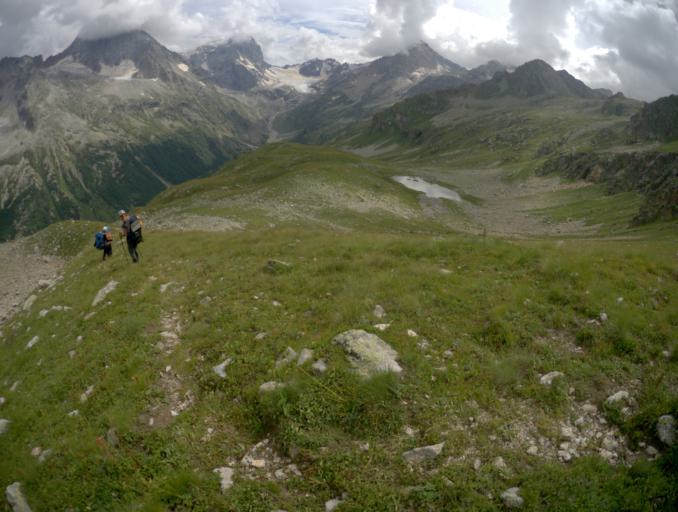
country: RU
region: Karachayevo-Cherkesiya
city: Uchkulan
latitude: 43.2708
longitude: 42.1263
